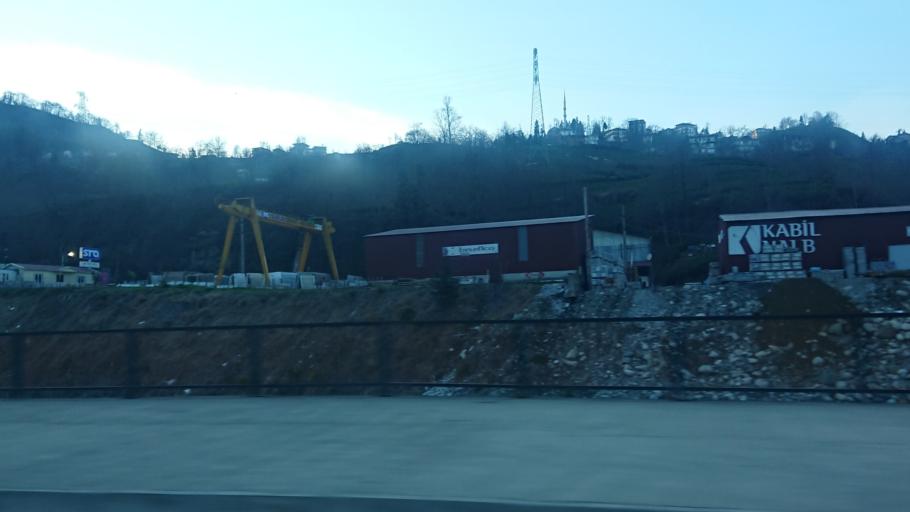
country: TR
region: Rize
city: Gundogdu
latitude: 41.0256
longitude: 40.5805
